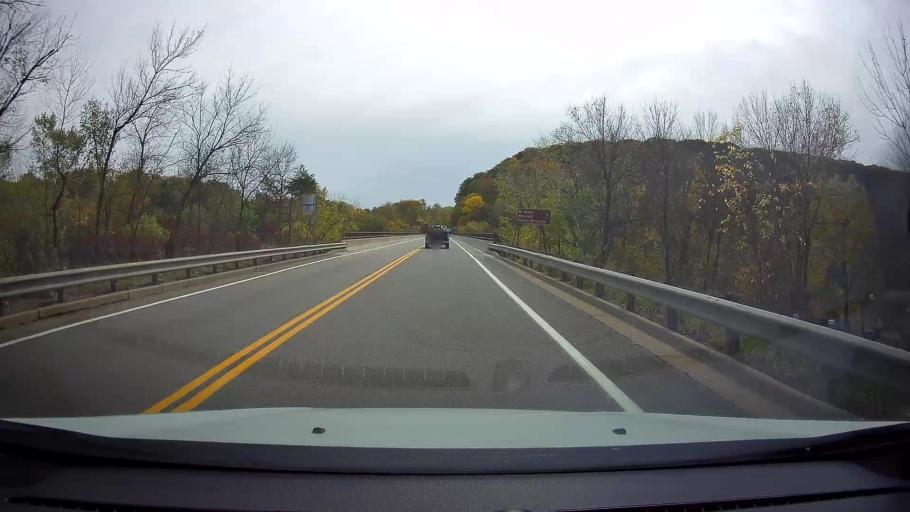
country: US
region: Wisconsin
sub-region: Polk County
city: Osceola
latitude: 45.3222
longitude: -92.7112
